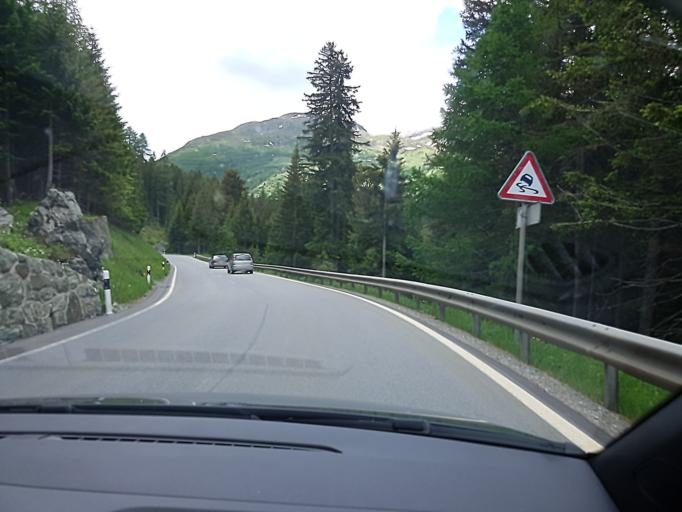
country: CH
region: Grisons
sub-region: Maloja District
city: Silvaplana
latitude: 46.4931
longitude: 9.6446
